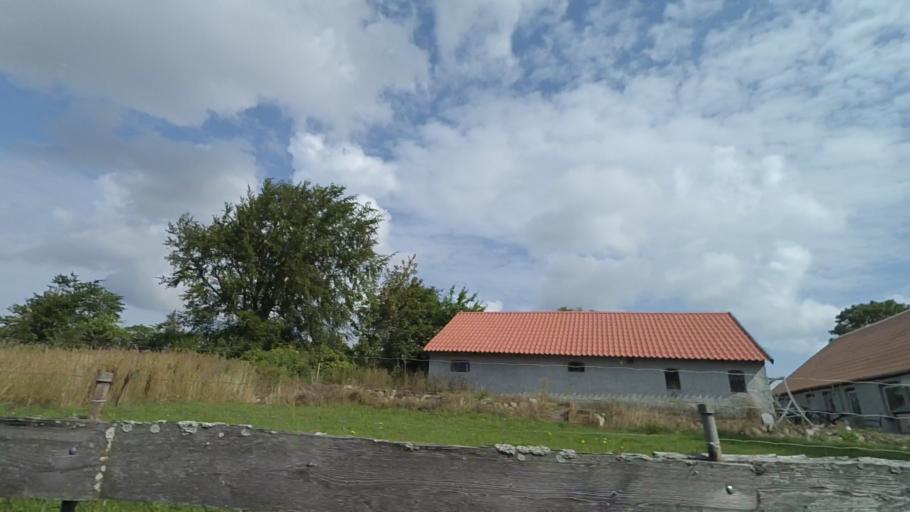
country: DK
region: Central Jutland
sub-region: Syddjurs Kommune
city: Ryomgard
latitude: 56.4773
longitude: 10.5036
